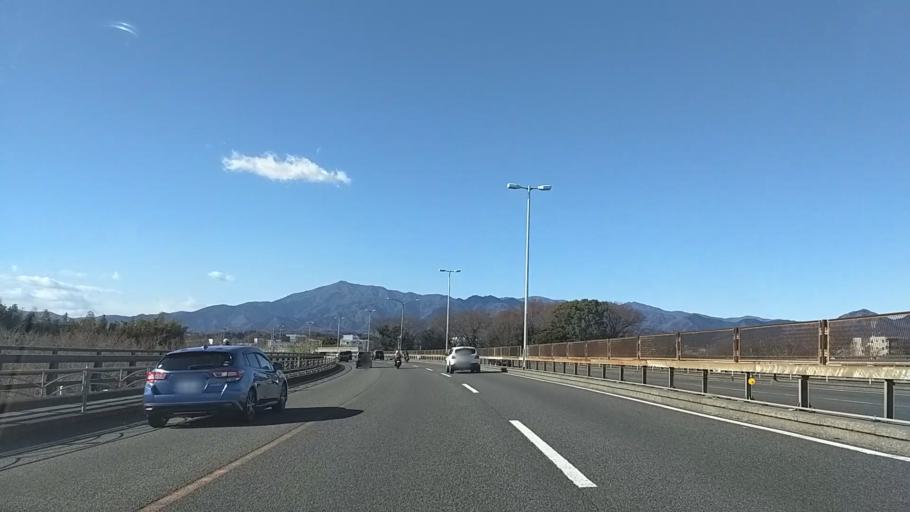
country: JP
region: Kanagawa
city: Atsugi
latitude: 35.4655
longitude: 139.3662
